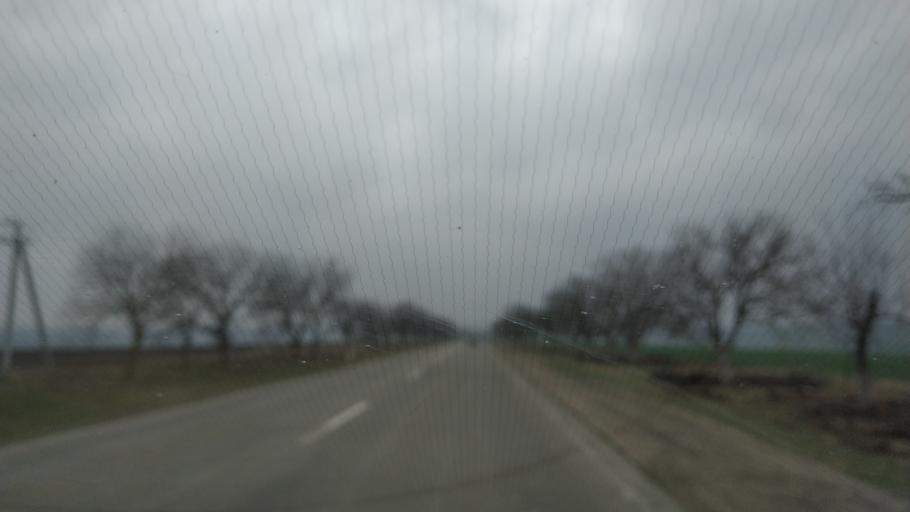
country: MD
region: Gagauzia
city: Comrat
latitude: 46.2595
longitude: 28.7504
